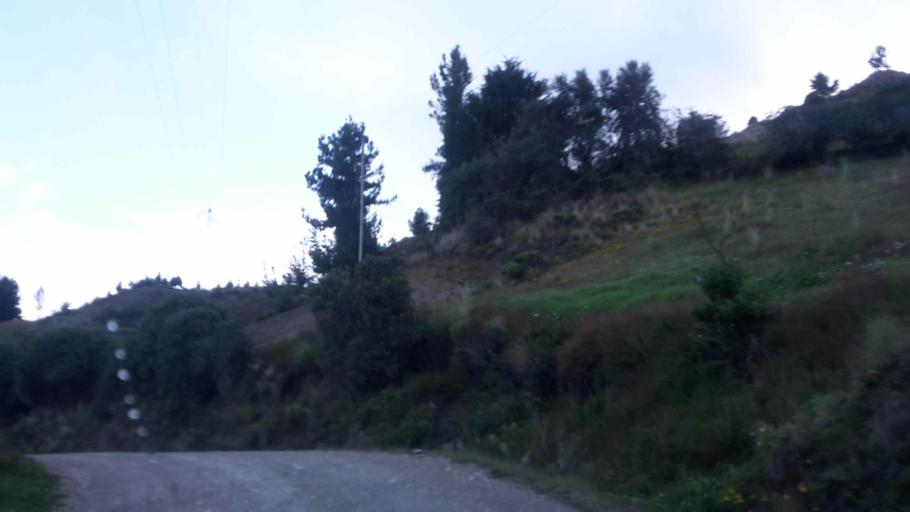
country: BO
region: Cochabamba
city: Colomi
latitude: -17.2502
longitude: -65.9051
